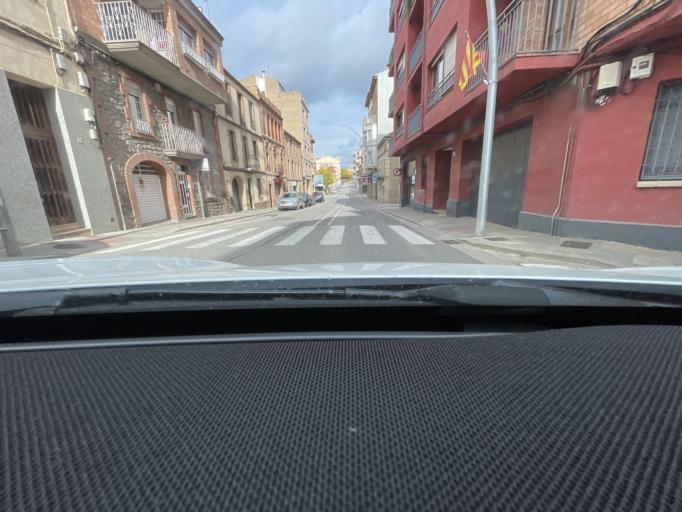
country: ES
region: Catalonia
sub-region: Provincia de Lleida
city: Solsona
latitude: 41.9920
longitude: 1.5128
